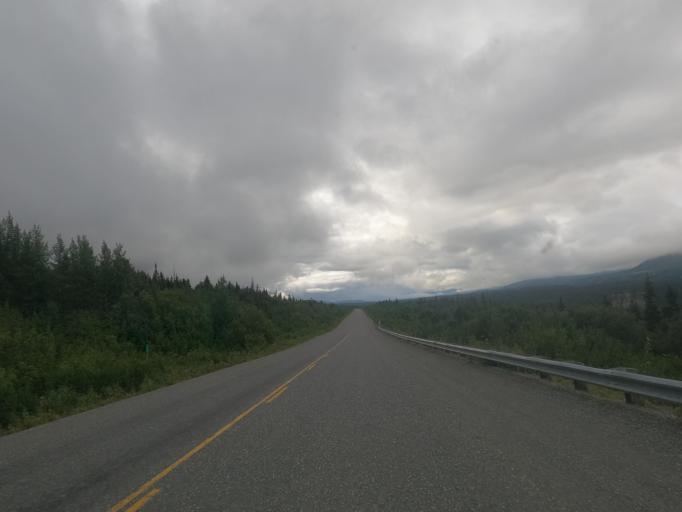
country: CA
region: Yukon
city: Haines Junction
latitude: 60.0362
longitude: -136.8811
